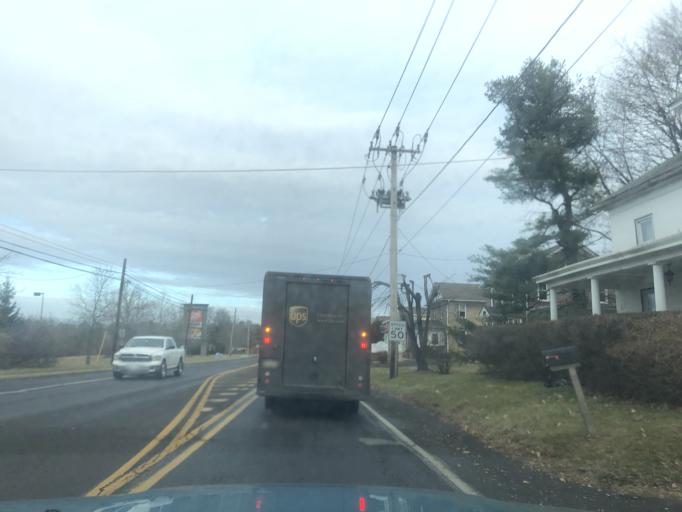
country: US
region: Pennsylvania
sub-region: Montgomery County
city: Souderton
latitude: 40.3224
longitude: -75.3034
